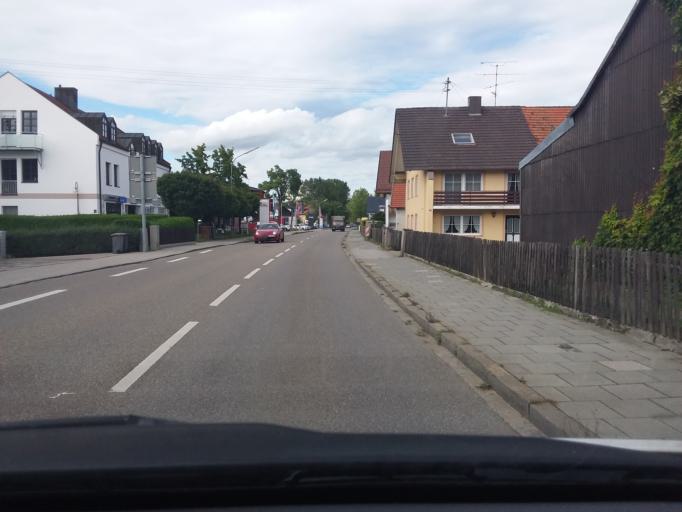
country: DE
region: Bavaria
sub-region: Upper Bavaria
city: Ismaning
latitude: 48.2303
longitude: 11.6760
